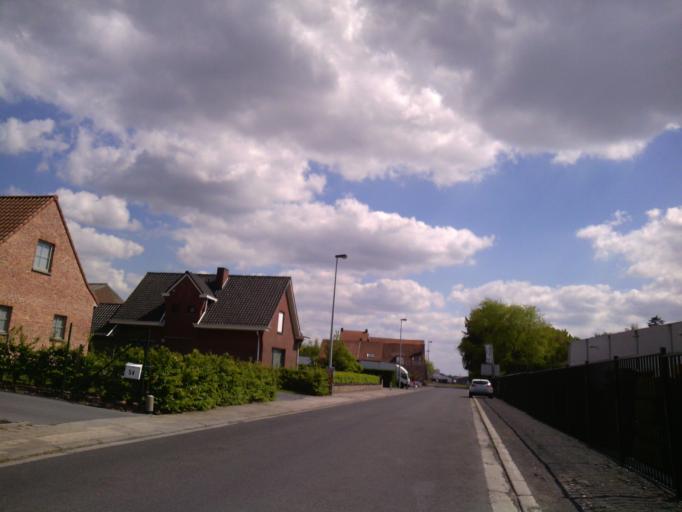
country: BE
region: Flanders
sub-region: Provincie West-Vlaanderen
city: Wevelgem
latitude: 50.7922
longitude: 3.1710
